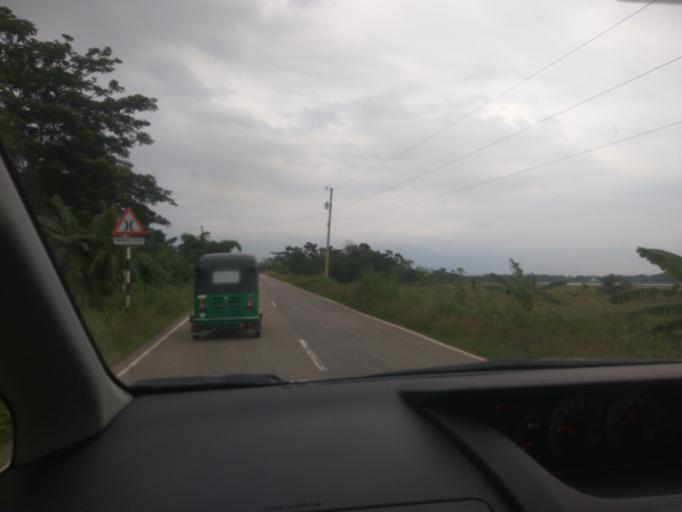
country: IN
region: Assam
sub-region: Karimganj
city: Karimganj
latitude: 24.9448
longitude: 92.2335
